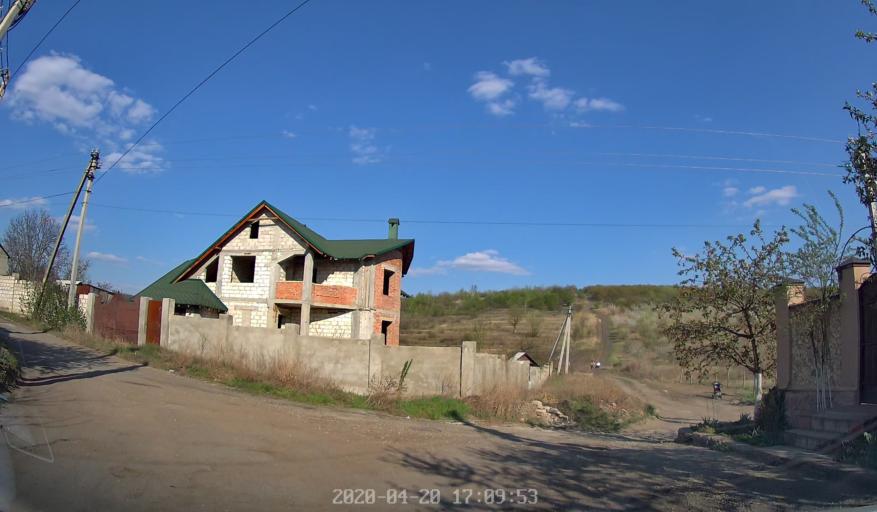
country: MD
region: Chisinau
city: Chisinau
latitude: 46.9610
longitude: 28.8402
